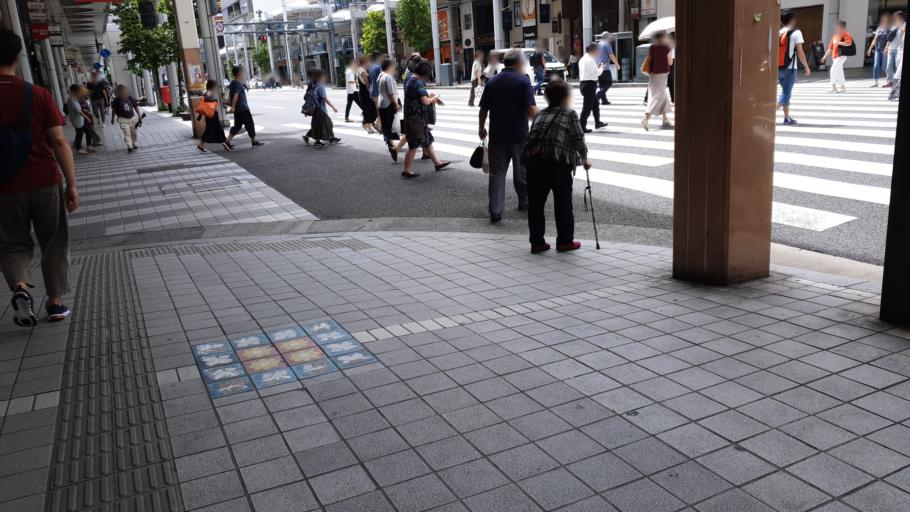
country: JP
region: Hiroshima
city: Hiroshima-shi
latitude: 34.3931
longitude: 132.4632
